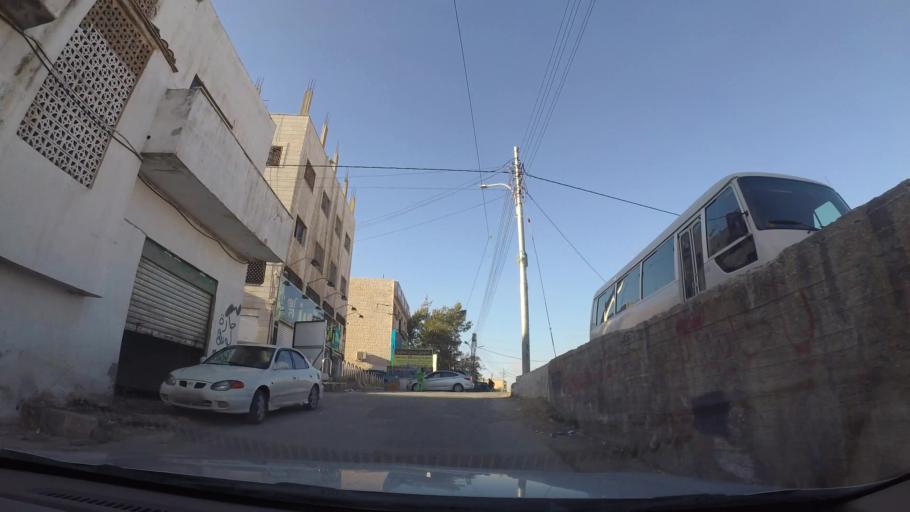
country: JO
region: Amman
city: Al Bunayyat ash Shamaliyah
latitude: 31.8998
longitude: 35.9120
